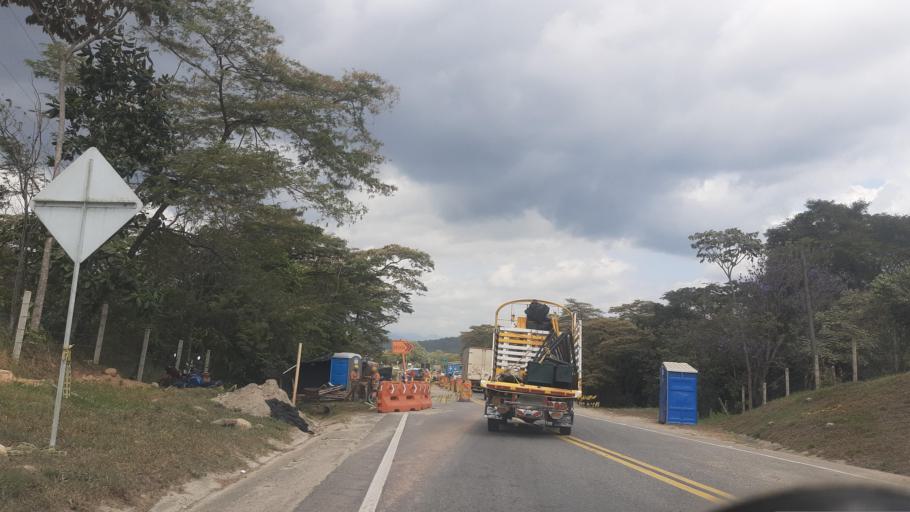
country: CO
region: Casanare
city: Tauramena
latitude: 4.9934
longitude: -72.6852
